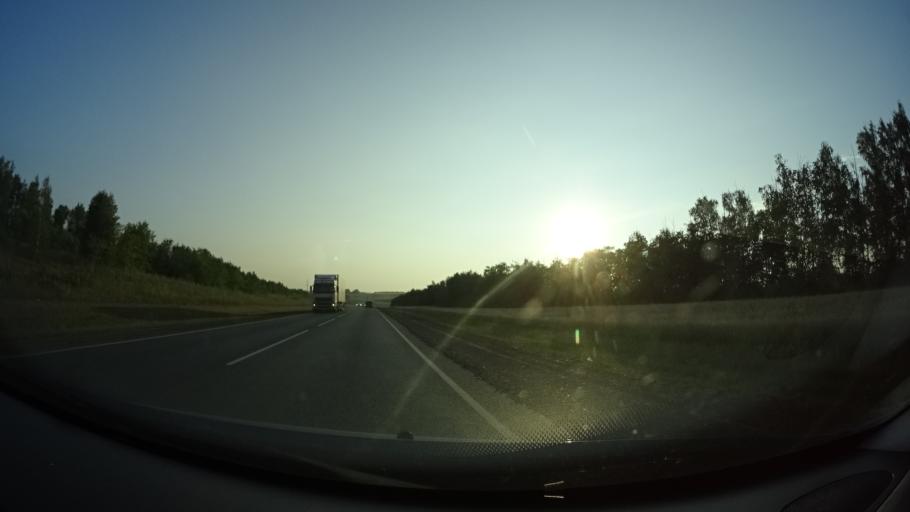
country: RU
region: Samara
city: Klyavlino
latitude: 54.0229
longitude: 51.8458
